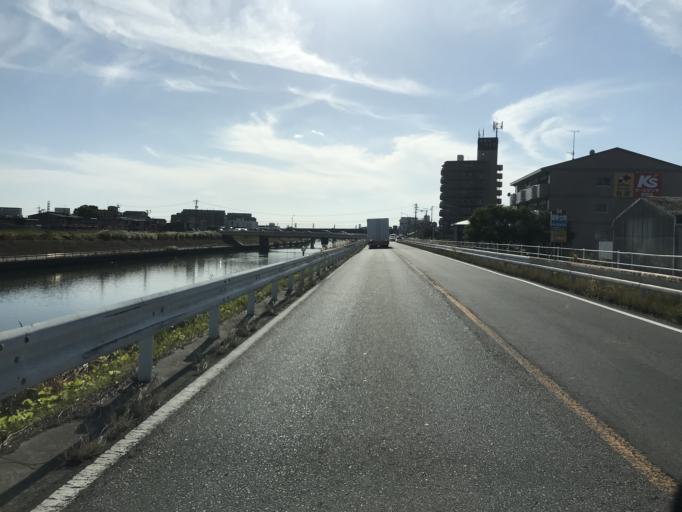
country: JP
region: Aichi
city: Nagoya-shi
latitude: 35.2075
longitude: 136.8594
